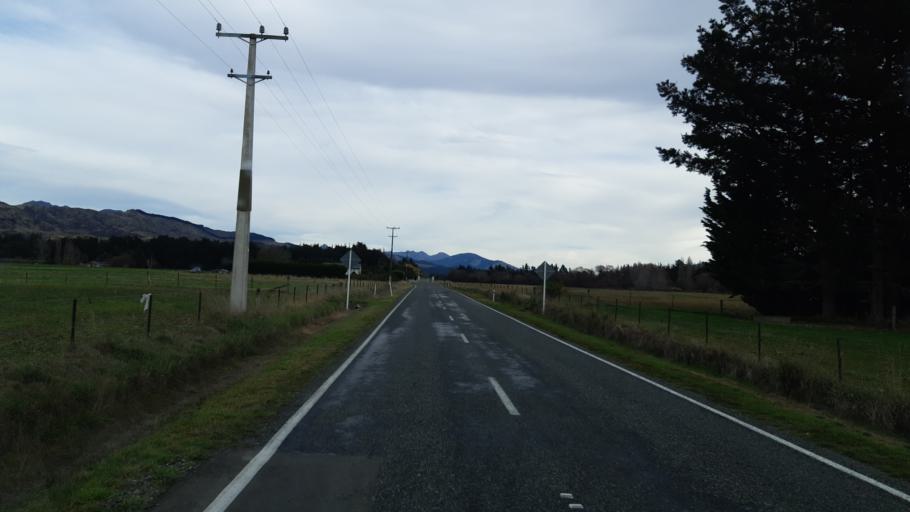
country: NZ
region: Tasman
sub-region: Tasman District
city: Brightwater
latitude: -41.6296
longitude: 173.3336
